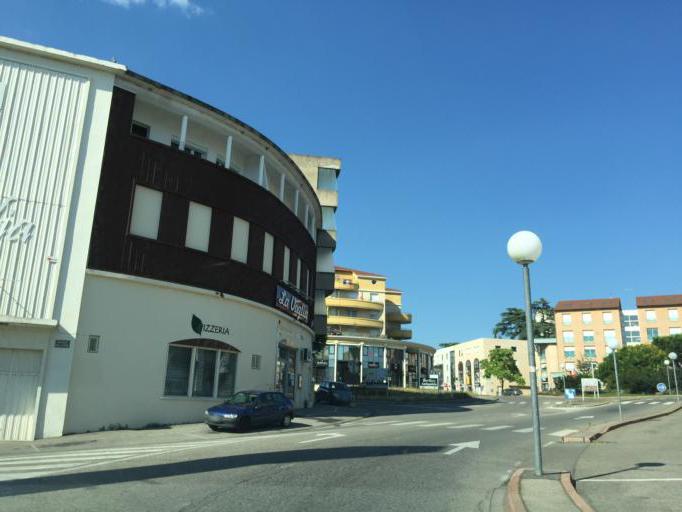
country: FR
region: Rhone-Alpes
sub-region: Departement de l'Ardeche
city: Annonay
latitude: 45.2446
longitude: 4.6737
